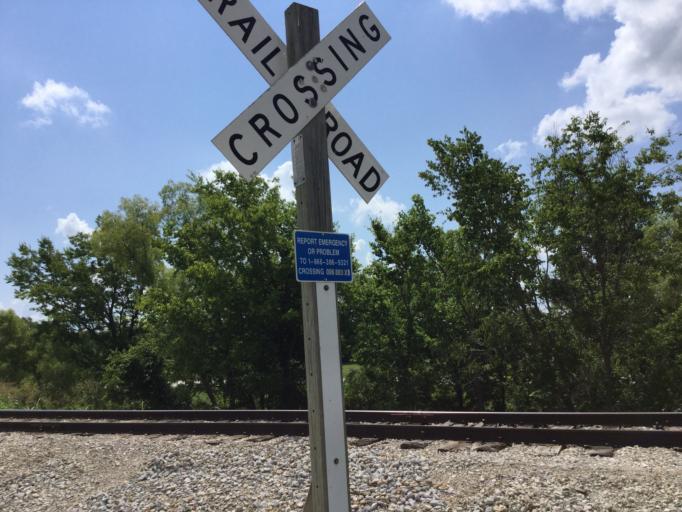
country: US
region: Kansas
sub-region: Montgomery County
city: Caney
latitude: 37.1106
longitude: -95.9052
